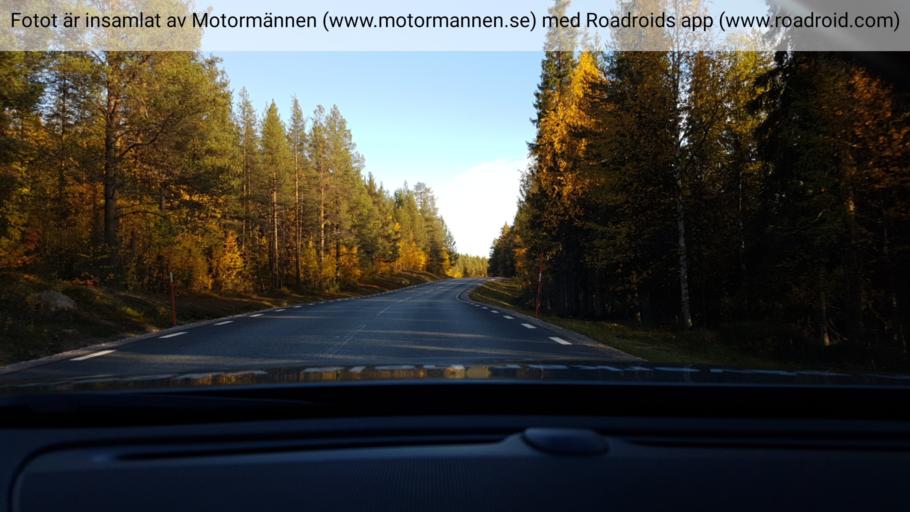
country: SE
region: Norrbotten
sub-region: Jokkmokks Kommun
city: Jokkmokk
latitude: 66.9399
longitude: 19.8055
